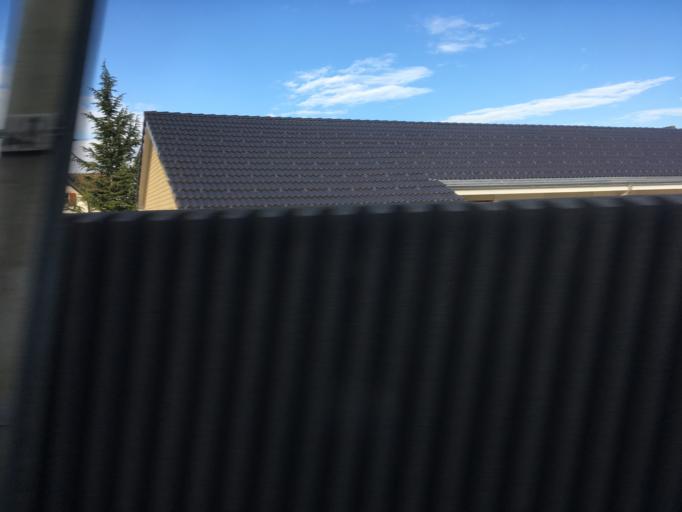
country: CH
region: Schwyz
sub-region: Bezirk Hoefe
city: Wollerau
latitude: 47.2001
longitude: 8.7236
